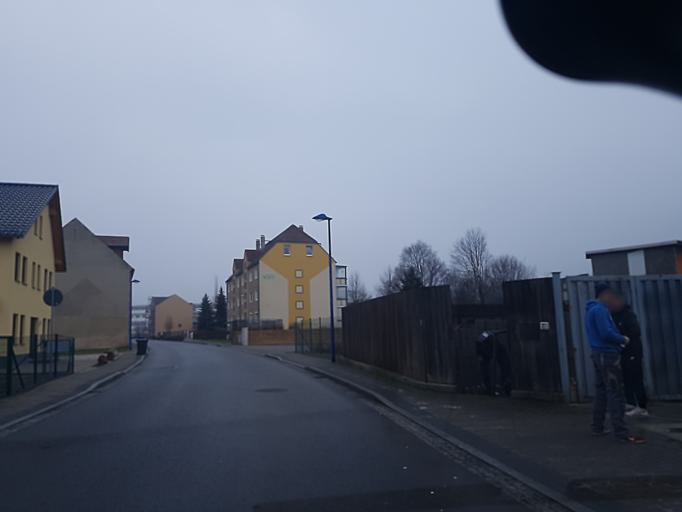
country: DE
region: Brandenburg
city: Finsterwalde
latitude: 51.6243
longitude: 13.7047
